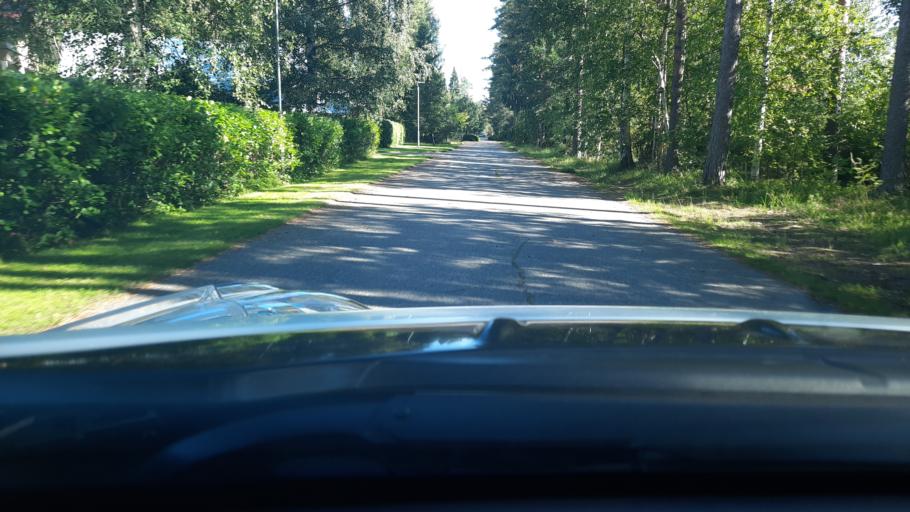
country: FI
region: North Karelia
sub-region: Joensuu
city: Joensuu
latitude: 62.6330
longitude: 29.6838
